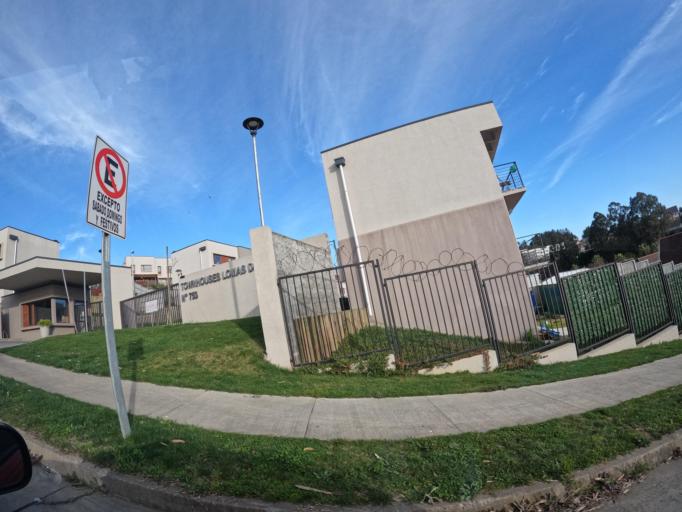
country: CL
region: Biobio
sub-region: Provincia de Concepcion
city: Concepcion
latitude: -36.7890
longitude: -73.0497
